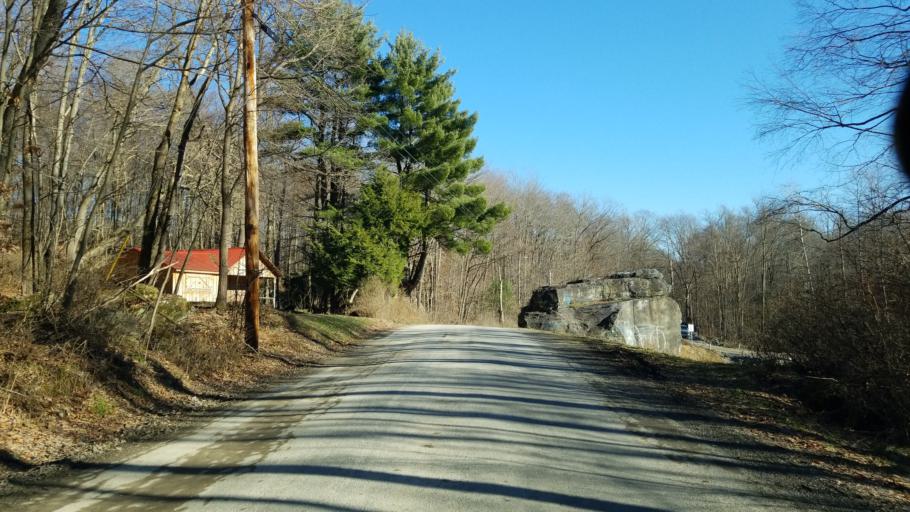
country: US
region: Pennsylvania
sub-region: Jefferson County
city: Falls Creek
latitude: 41.1597
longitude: -78.8389
